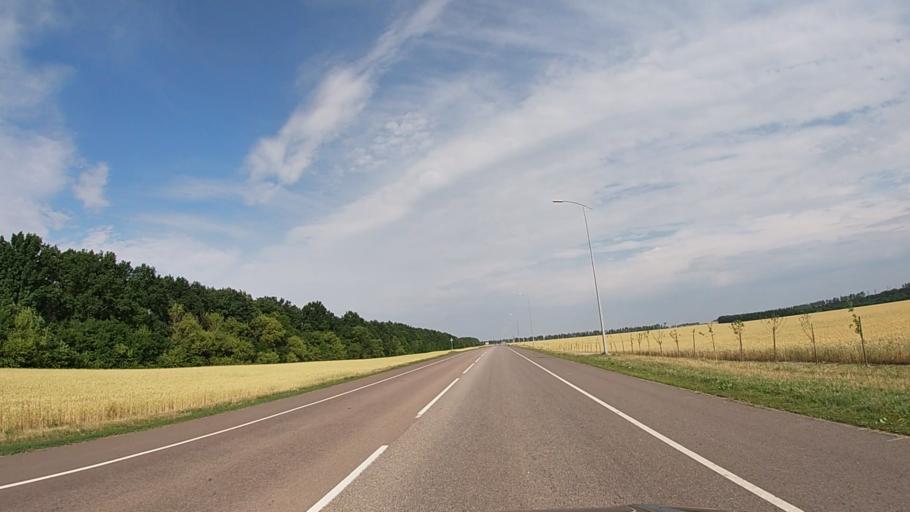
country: RU
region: Belgorod
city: Proletarskiy
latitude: 50.8255
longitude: 35.7802
